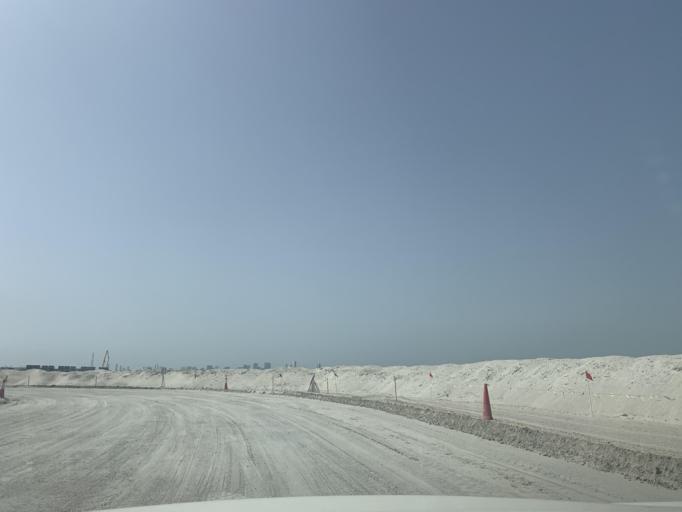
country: BH
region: Northern
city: Sitrah
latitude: 26.1615
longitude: 50.6402
